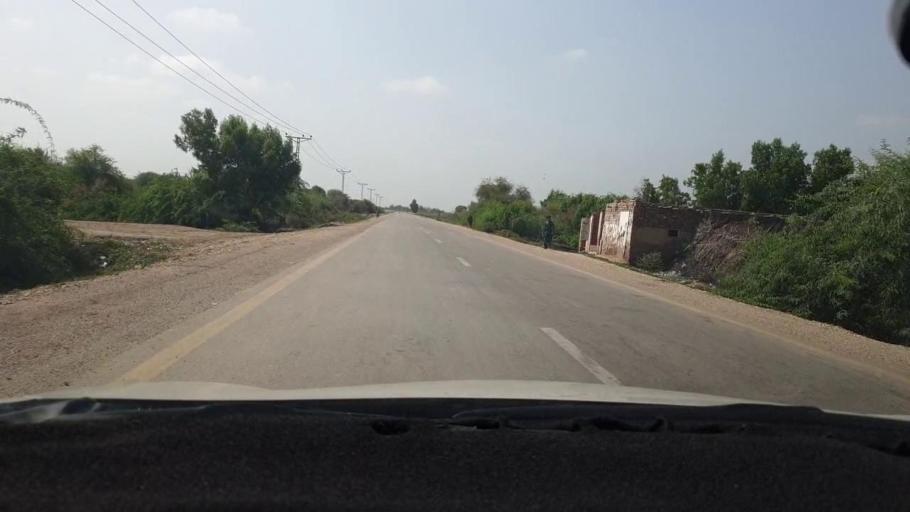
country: PK
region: Sindh
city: Mirpur Khas
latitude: 25.7536
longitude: 69.0846
